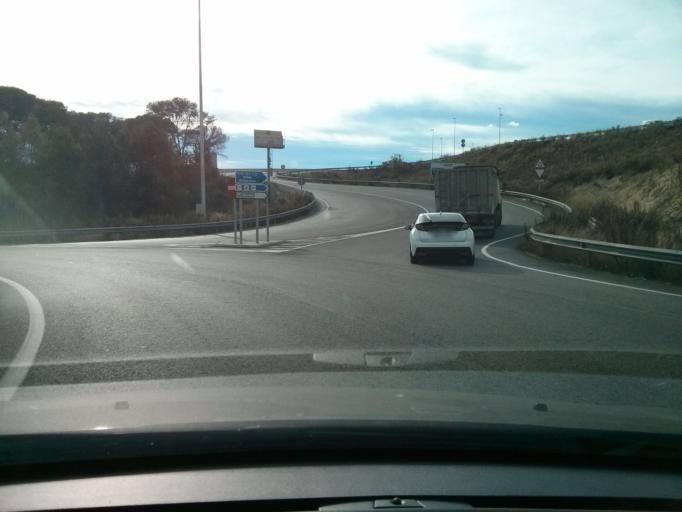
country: ES
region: Catalonia
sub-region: Provincia de Tarragona
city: Constanti
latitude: 41.1425
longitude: 1.2337
